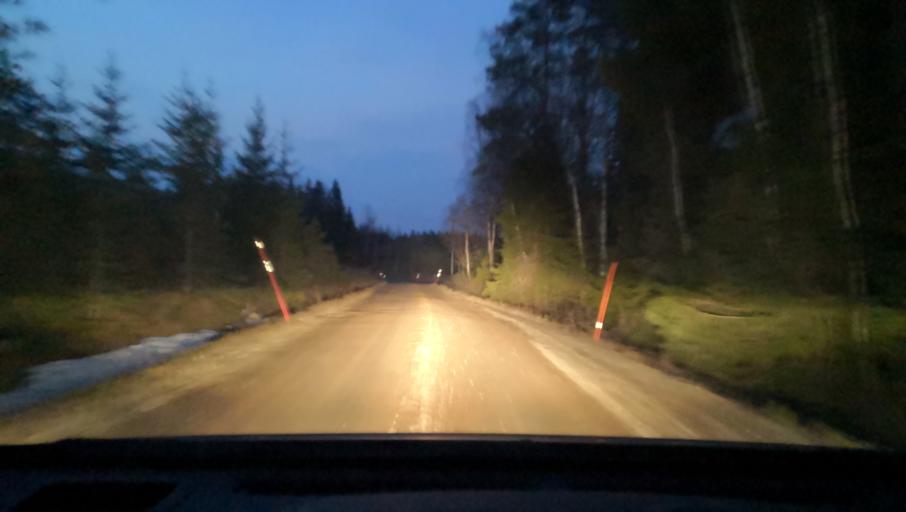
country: SE
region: OErebro
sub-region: Lindesbergs Kommun
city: Frovi
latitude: 59.6106
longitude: 15.4783
